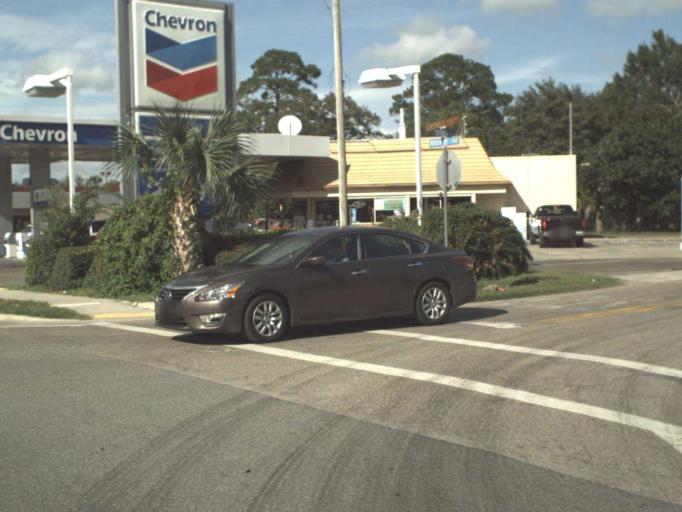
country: US
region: Florida
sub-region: Gulf County
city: Port Saint Joe
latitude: 29.8095
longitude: -85.3024
